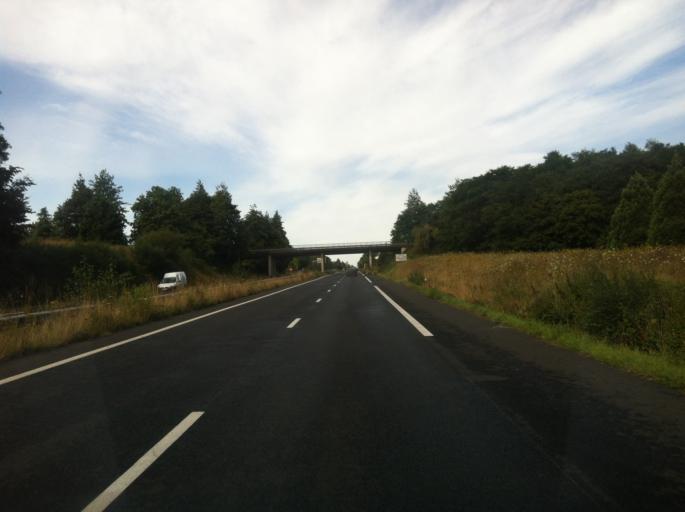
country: FR
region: Brittany
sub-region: Departement des Cotes-d'Armor
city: Belle-Isle-en-Terre
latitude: 48.5498
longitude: -3.4041
